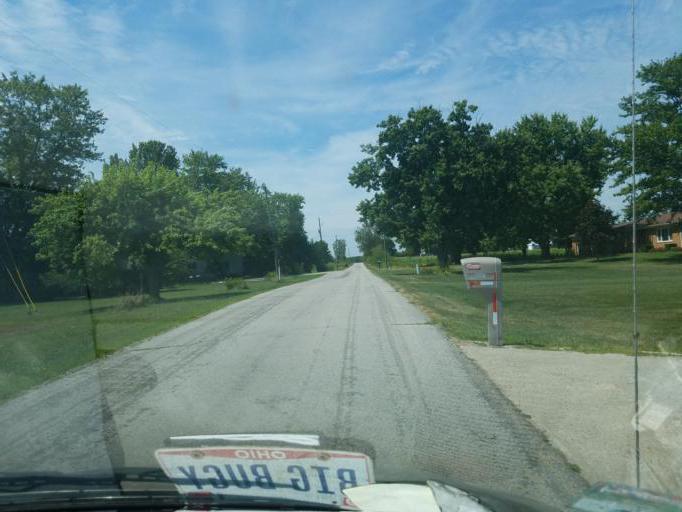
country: US
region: Ohio
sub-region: Franklin County
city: Lake Darby
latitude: 39.8771
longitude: -83.2007
